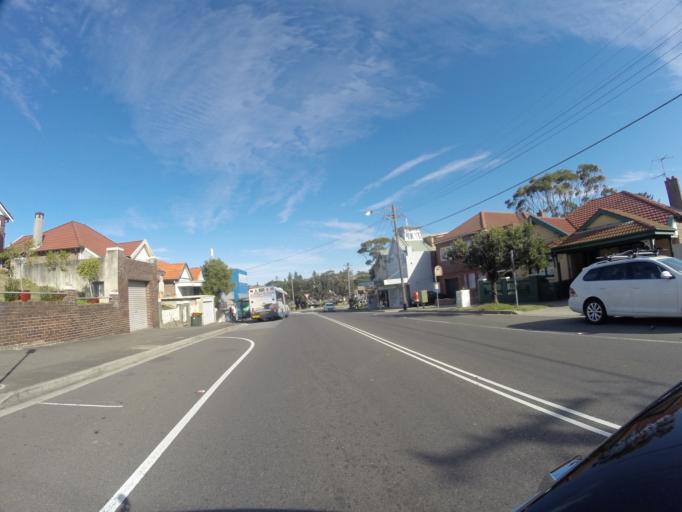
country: AU
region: New South Wales
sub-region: Randwick
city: South Coogee
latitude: -33.9281
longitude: 151.2553
